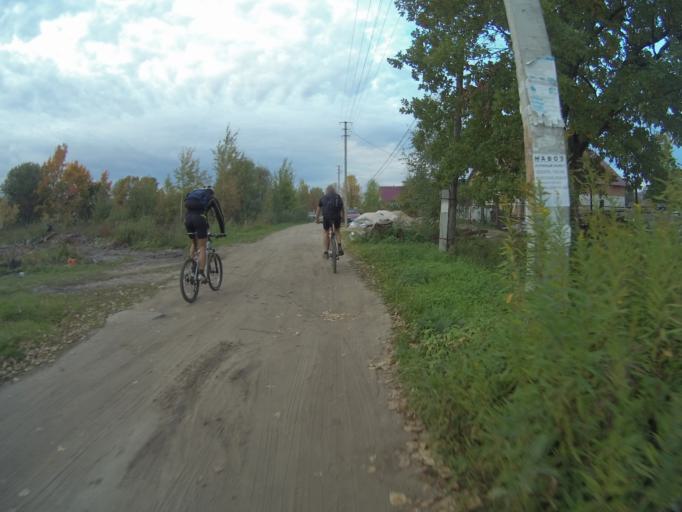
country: RU
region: Vladimir
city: Sobinka
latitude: 55.9854
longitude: 40.0094
